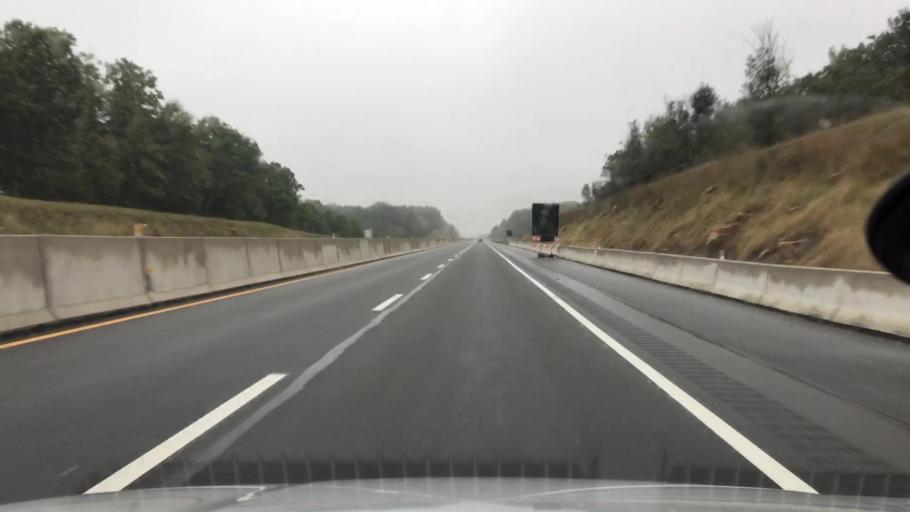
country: US
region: Pennsylvania
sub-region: Luzerne County
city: White Haven
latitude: 41.1465
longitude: -75.7760
